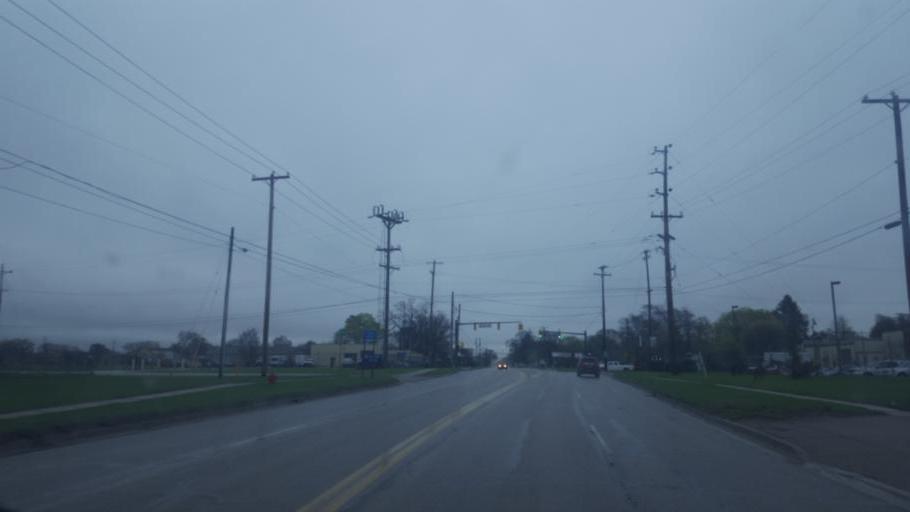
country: US
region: Michigan
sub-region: Isabella County
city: Mount Pleasant
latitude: 43.6118
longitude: -84.7782
